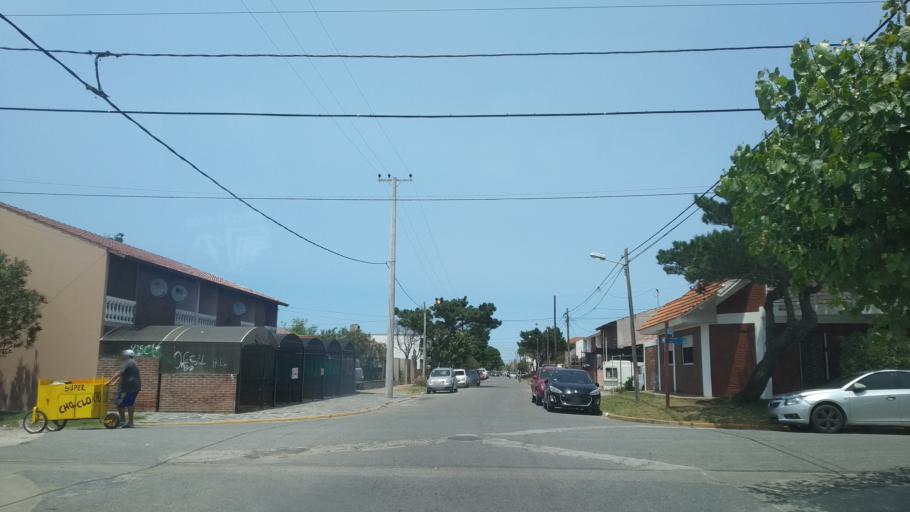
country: AR
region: Buenos Aires
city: Mar del Tuyu
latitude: -36.5600
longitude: -56.6894
